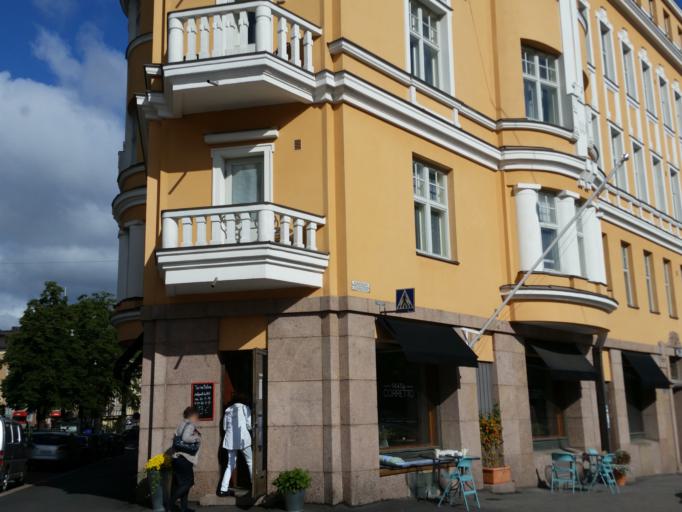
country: FI
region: Uusimaa
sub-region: Helsinki
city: Helsinki
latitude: 60.1733
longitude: 24.9318
